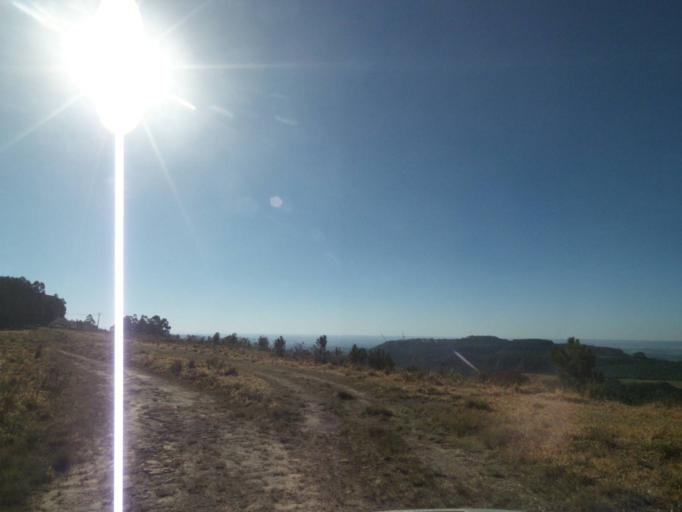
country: BR
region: Parana
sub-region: Tibagi
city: Tibagi
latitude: -24.5771
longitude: -50.4820
